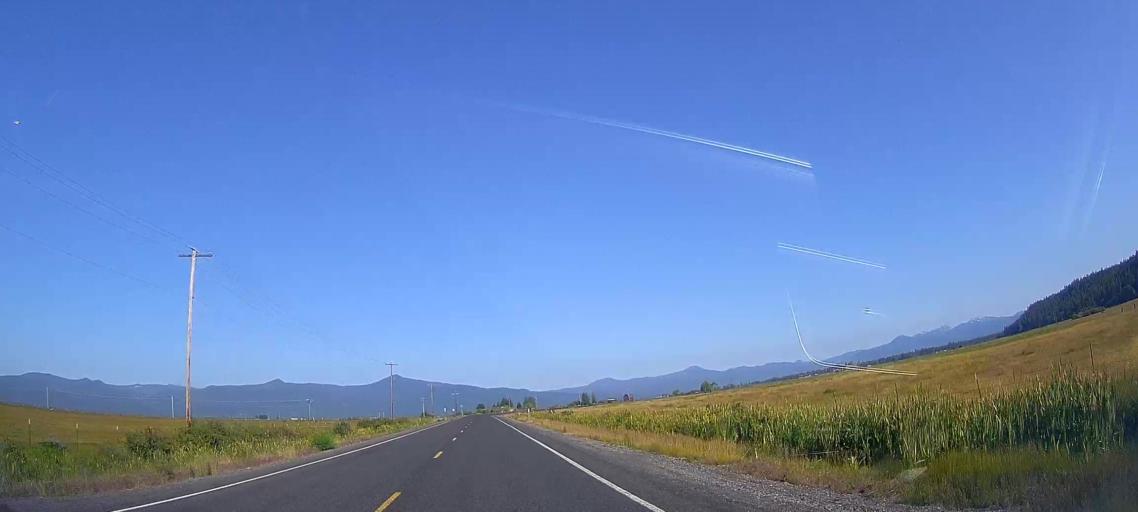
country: US
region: Oregon
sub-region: Klamath County
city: Klamath Falls
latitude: 42.6455
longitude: -121.9495
